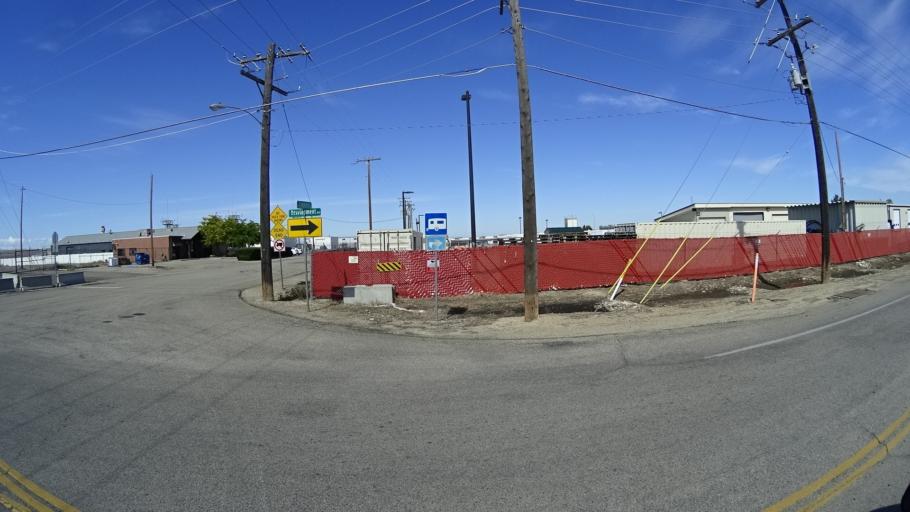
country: US
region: Idaho
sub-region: Ada County
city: Boise
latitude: 43.5644
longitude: -116.2074
